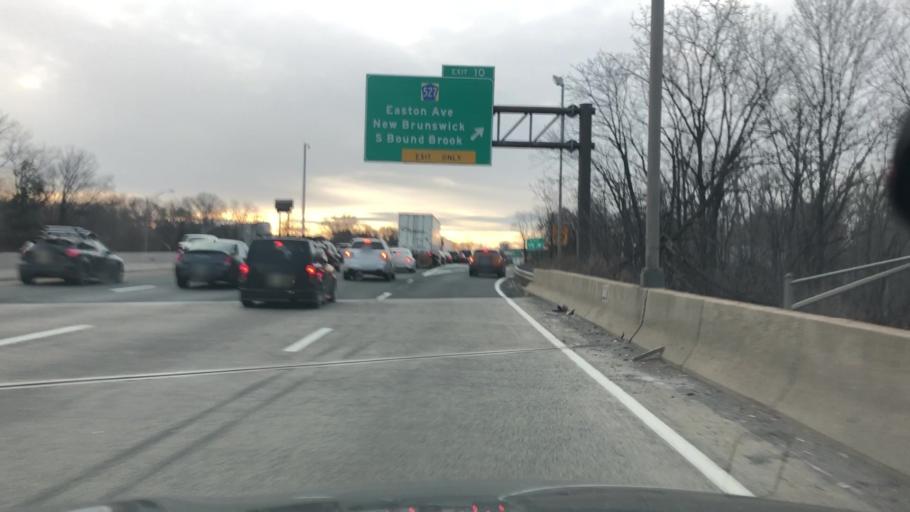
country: US
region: New Jersey
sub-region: Somerset County
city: South Bound Brook
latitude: 40.5396
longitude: -74.5131
